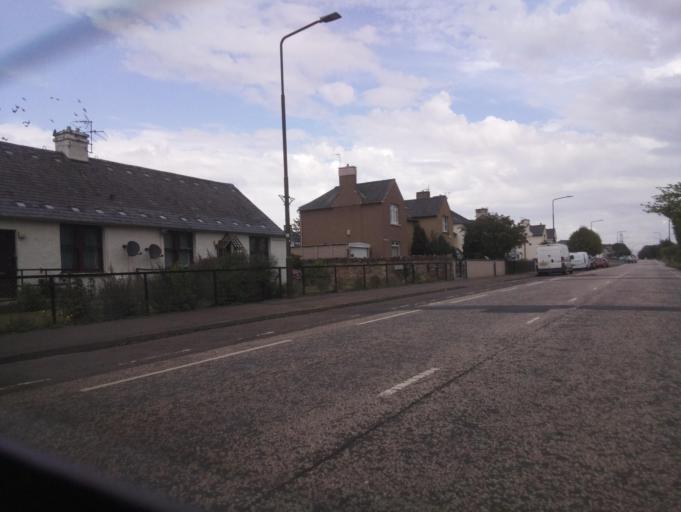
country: GB
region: Scotland
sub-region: East Lothian
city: Prestonpans
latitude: 55.9543
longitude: -2.9698
